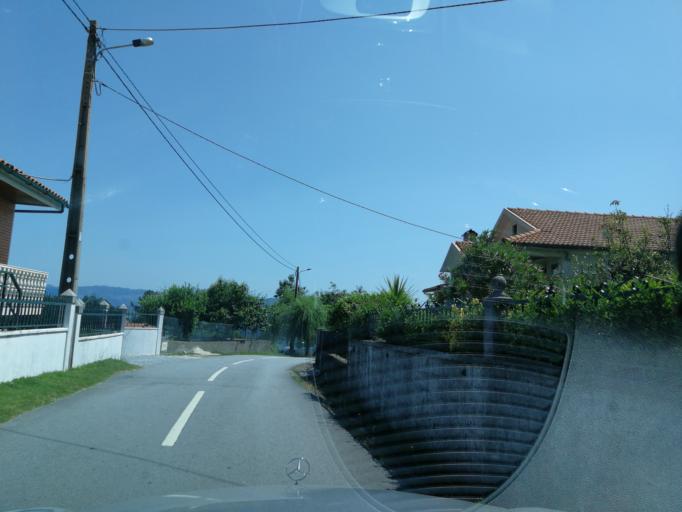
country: PT
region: Braga
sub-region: Povoa de Lanhoso
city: Povoa de Lanhoso
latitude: 41.5807
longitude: -8.3248
